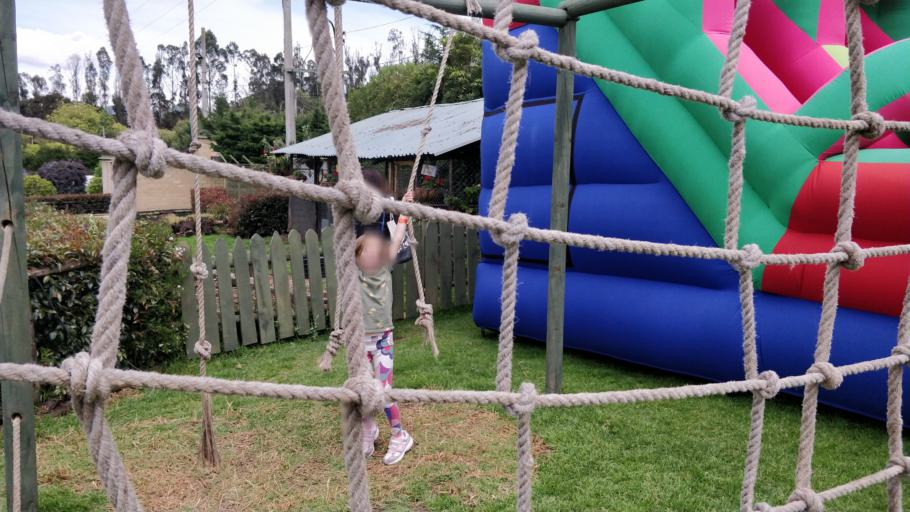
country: CO
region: Cundinamarca
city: La Calera
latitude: 4.7846
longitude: -73.9512
